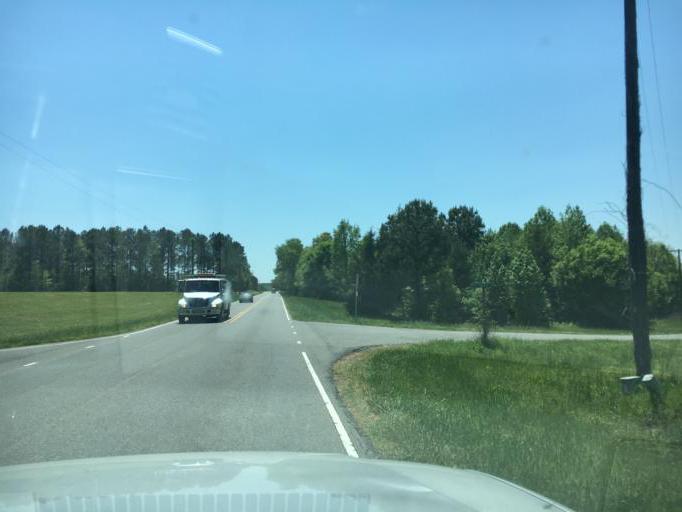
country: US
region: South Carolina
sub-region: Cherokee County
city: Blacksburg
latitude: 35.1939
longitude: -81.5659
